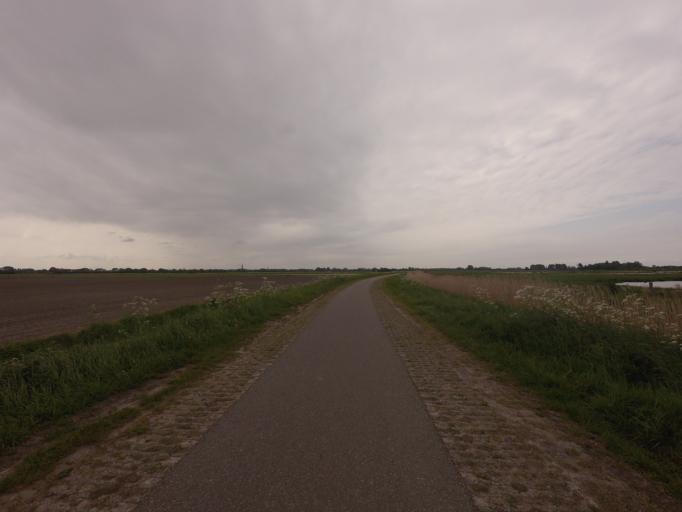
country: NL
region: Zeeland
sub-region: Gemeente Middelburg
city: Middelburg
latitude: 51.5219
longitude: 3.5874
